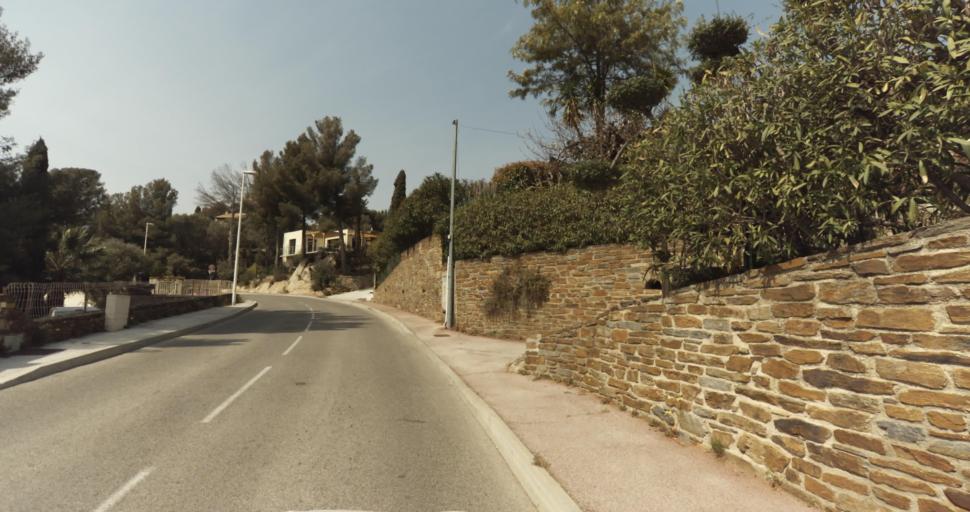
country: FR
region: Provence-Alpes-Cote d'Azur
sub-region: Departement du Var
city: Bormes-les-Mimosas
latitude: 43.1442
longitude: 6.3494
